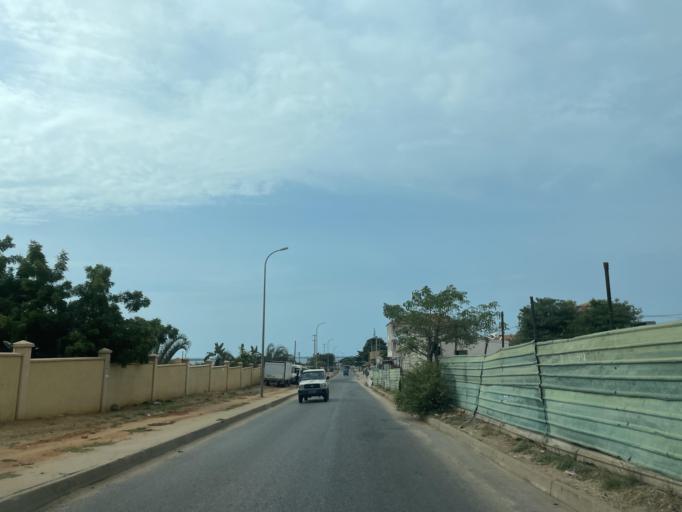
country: AO
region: Luanda
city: Luanda
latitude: -8.9191
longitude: 13.1694
